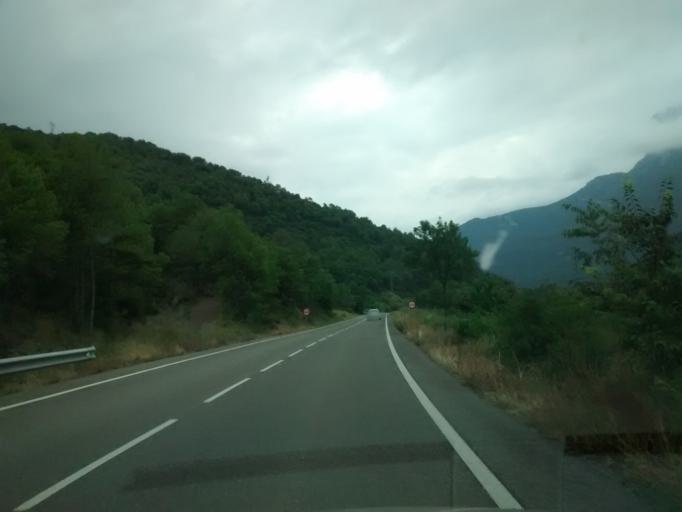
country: ES
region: Aragon
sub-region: Provincia de Huesca
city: Labuerda
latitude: 42.4637
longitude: 0.1365
